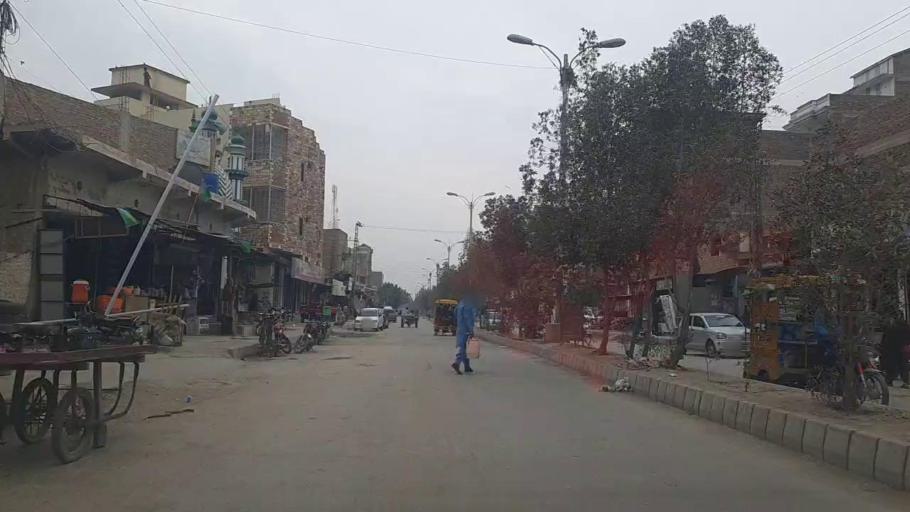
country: PK
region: Sindh
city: Nawabshah
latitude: 26.2577
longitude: 68.4009
